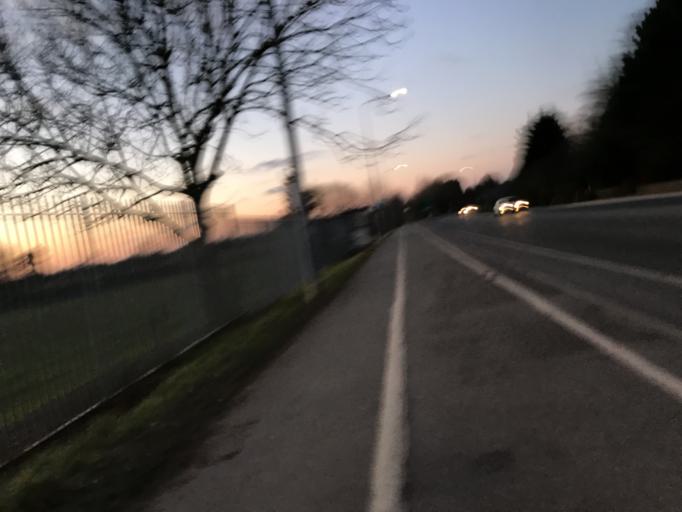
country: GB
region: England
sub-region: Lincolnshire
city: Holton le Clay
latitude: 53.5221
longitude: -0.0759
